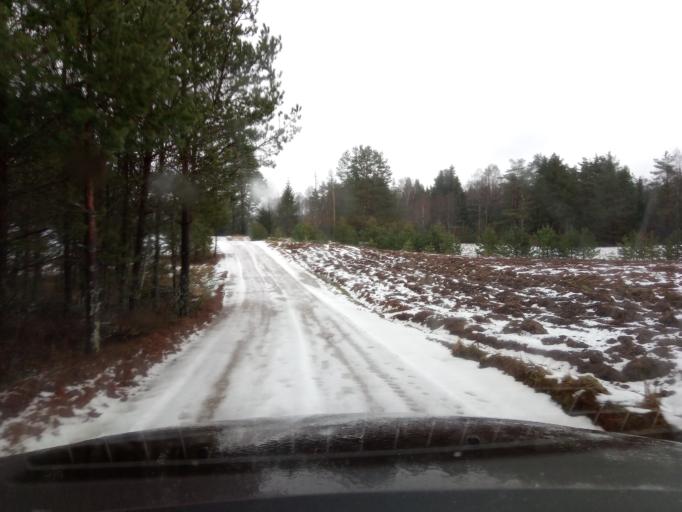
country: LT
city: Svencioneliai
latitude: 55.3363
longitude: 25.8060
